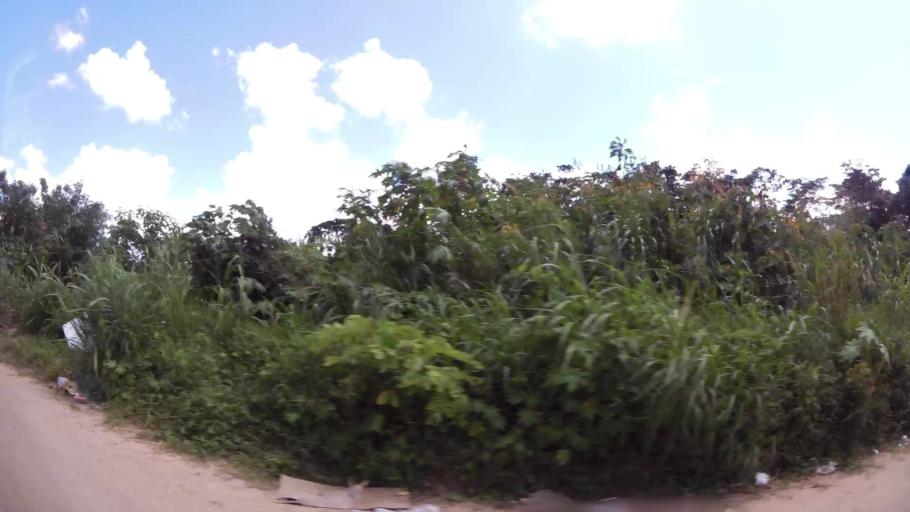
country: SR
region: Paramaribo
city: Paramaribo
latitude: 5.8607
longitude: -55.1522
